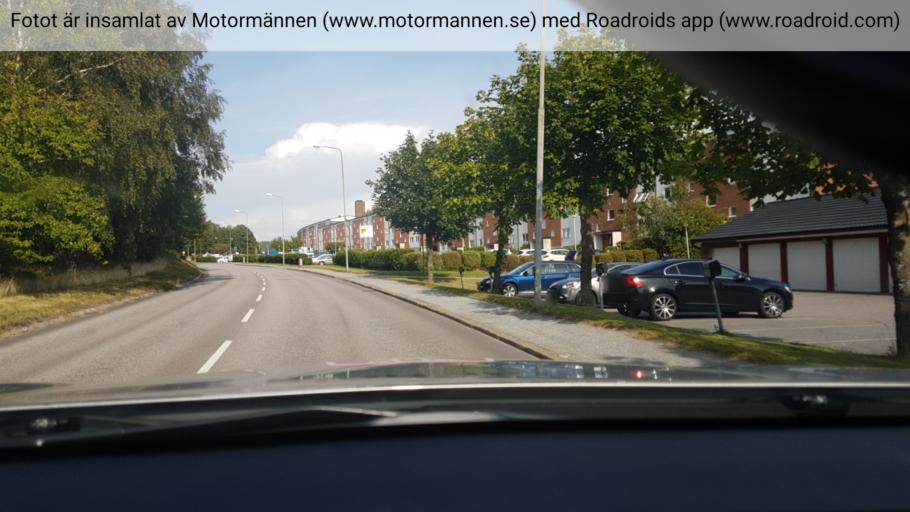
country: SE
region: Vaestra Goetaland
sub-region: Stenungsunds Kommun
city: Stenungsund
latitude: 58.0650
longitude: 11.8379
